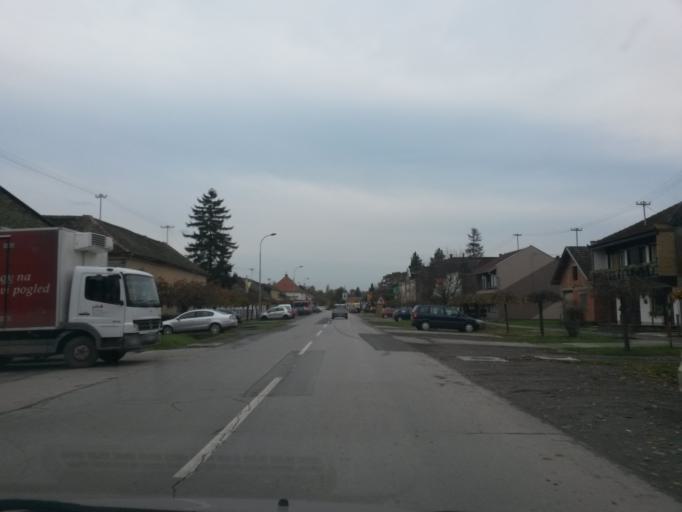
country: HR
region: Osjecko-Baranjska
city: Darda
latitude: 45.6269
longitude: 18.6866
